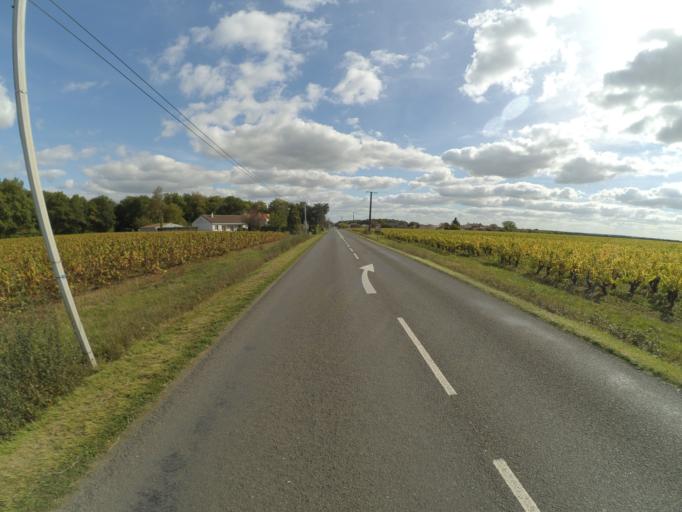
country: FR
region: Pays de la Loire
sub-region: Departement de la Loire-Atlantique
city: Saint-Lumine-de-Clisson
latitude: 47.1091
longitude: -1.3365
